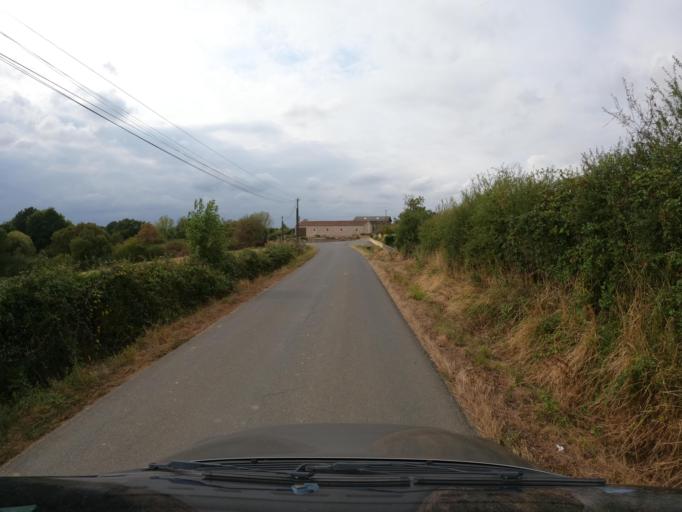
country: FR
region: Pays de la Loire
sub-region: Departement de Maine-et-Loire
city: Saint-Christophe-du-Bois
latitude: 47.0382
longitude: -0.9680
